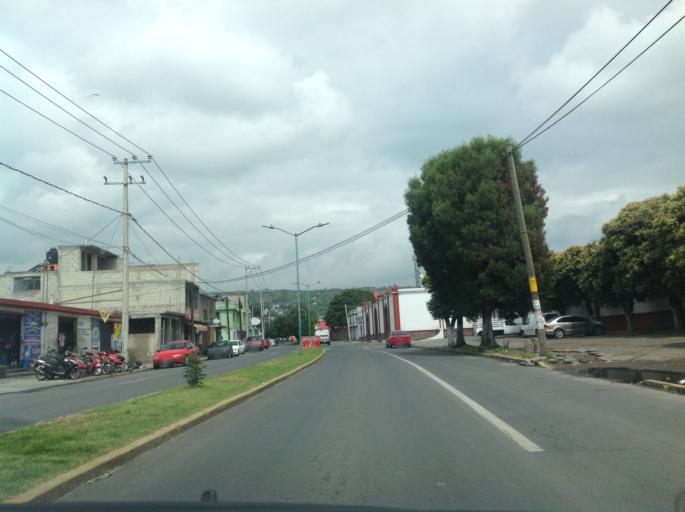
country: MX
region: Morelos
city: Tenango de Arista
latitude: 19.1057
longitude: -99.5825
